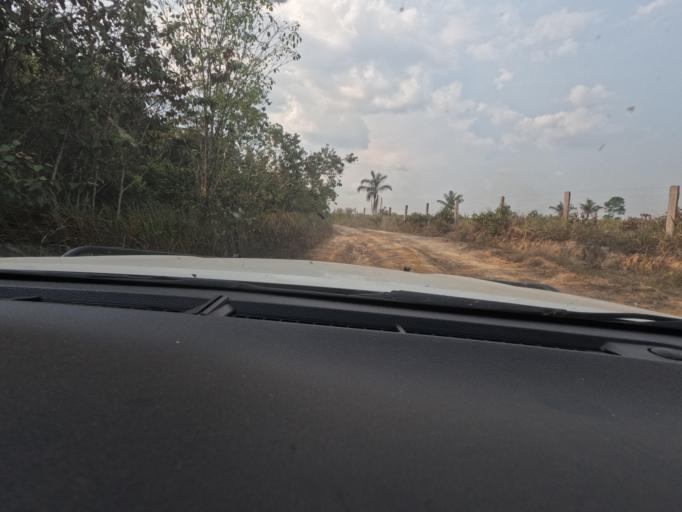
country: BR
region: Rondonia
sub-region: Porto Velho
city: Porto Velho
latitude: -8.6439
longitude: -63.1555
